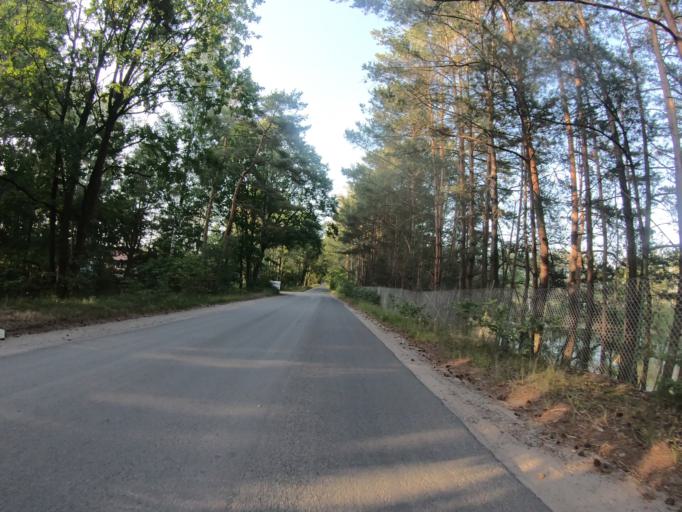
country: DE
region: Lower Saxony
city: Wagenhoff
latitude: 52.5248
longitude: 10.4809
